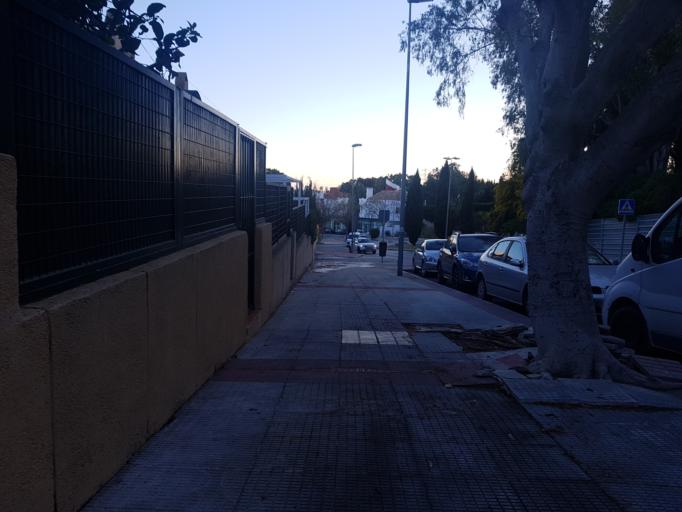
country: ES
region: Andalusia
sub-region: Provincia de Malaga
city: Marbella
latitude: 36.5240
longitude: -4.8918
